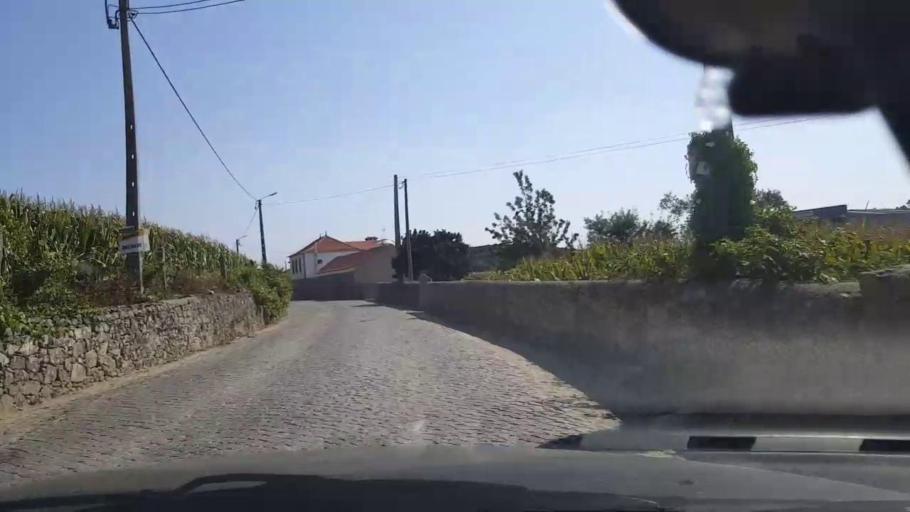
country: PT
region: Porto
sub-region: Povoa de Varzim
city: Pedroso
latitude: 41.4079
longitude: -8.6931
